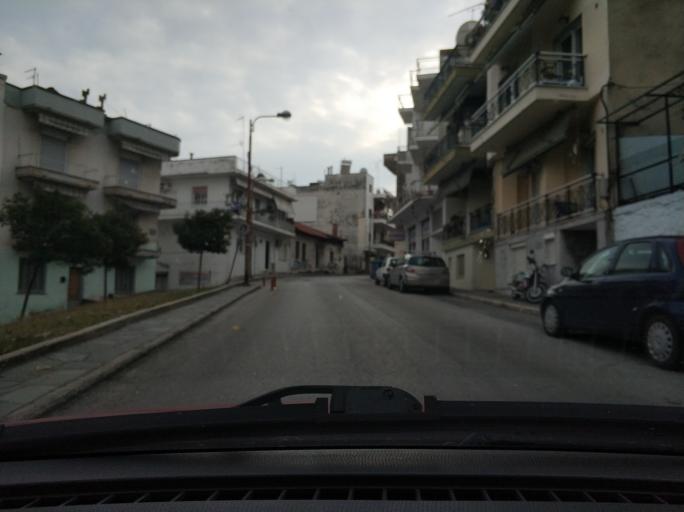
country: GR
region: East Macedonia and Thrace
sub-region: Nomos Kavalas
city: Kavala
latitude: 40.9413
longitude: 24.4200
